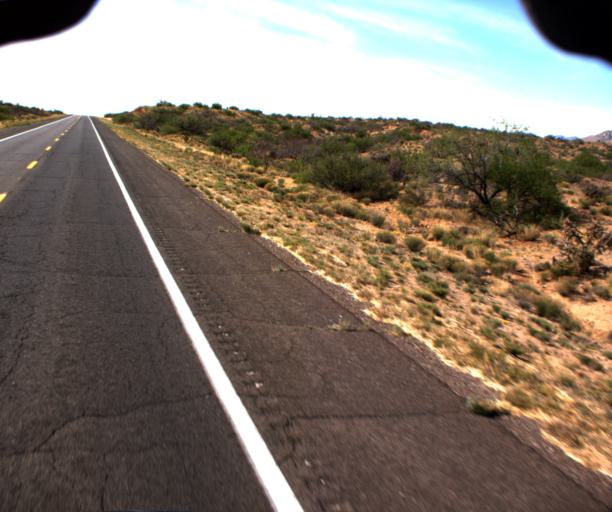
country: US
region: Arizona
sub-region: Graham County
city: Swift Trail Junction
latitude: 32.6320
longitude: -109.6919
